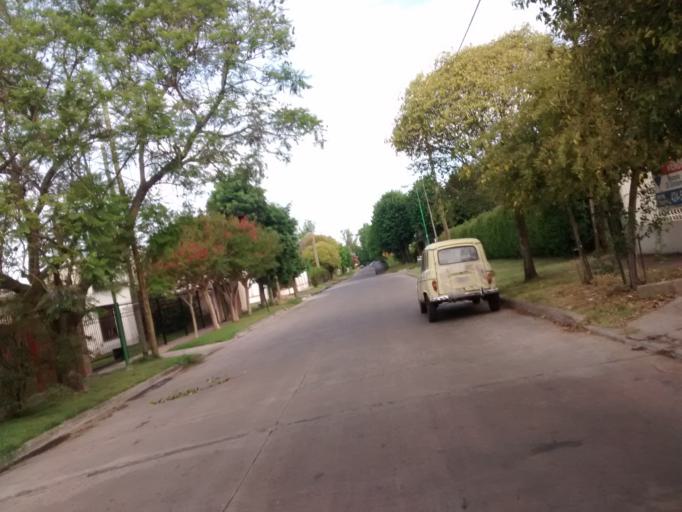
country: AR
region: Buenos Aires
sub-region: Partido de La Plata
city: La Plata
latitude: -34.8551
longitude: -58.0789
